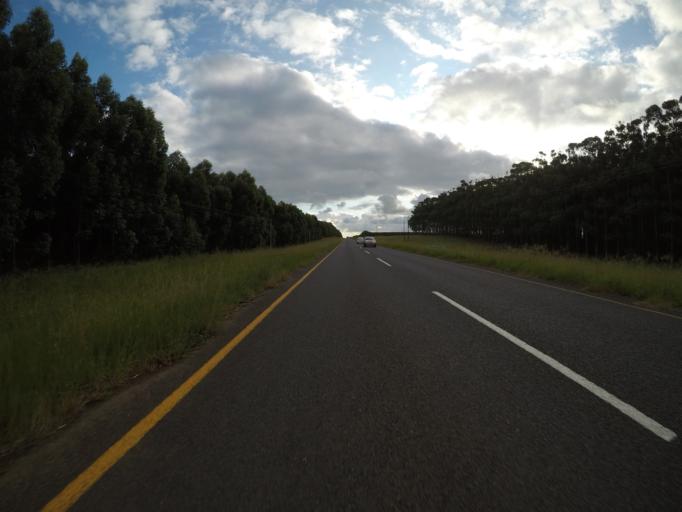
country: ZA
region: KwaZulu-Natal
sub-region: uMkhanyakude District Municipality
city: Mtubatuba
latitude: -28.3879
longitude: 32.2326
